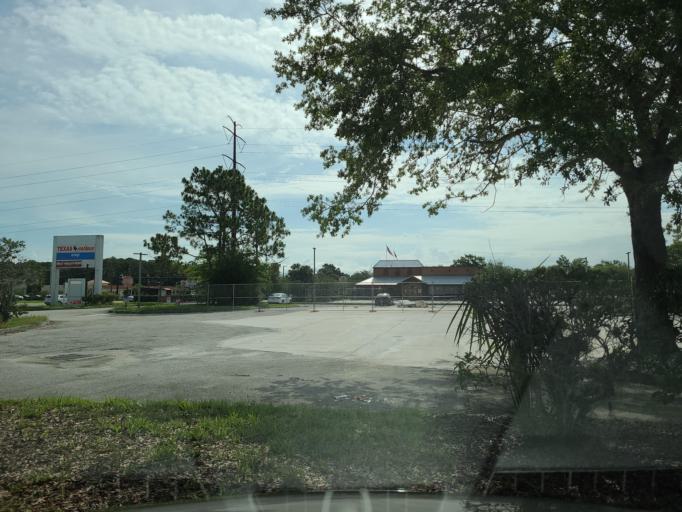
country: US
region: Florida
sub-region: Seminole County
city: Lake Mary
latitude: 28.8107
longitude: -81.3359
